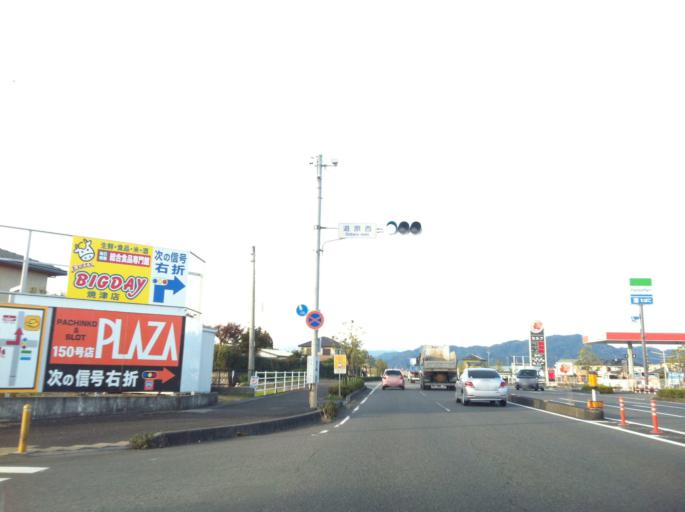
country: JP
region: Shizuoka
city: Yaizu
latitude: 34.8365
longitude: 138.3003
